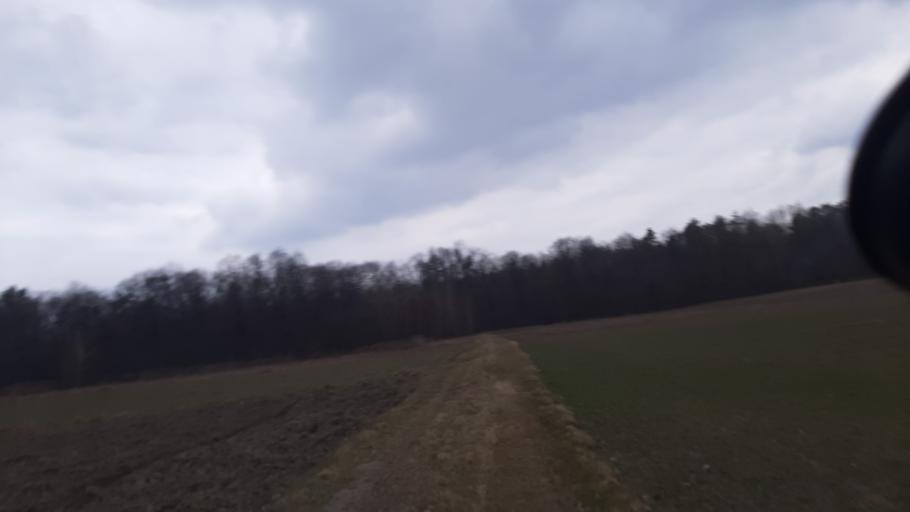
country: PL
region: Lublin Voivodeship
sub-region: Powiat lubelski
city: Garbow
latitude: 51.3925
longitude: 22.4002
